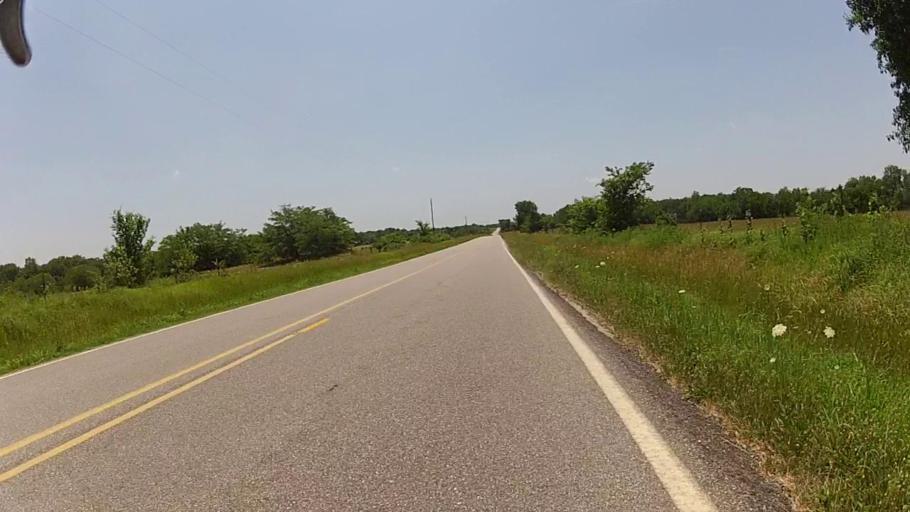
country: US
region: Kansas
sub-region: Montgomery County
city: Cherryvale
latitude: 37.2340
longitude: -95.5377
